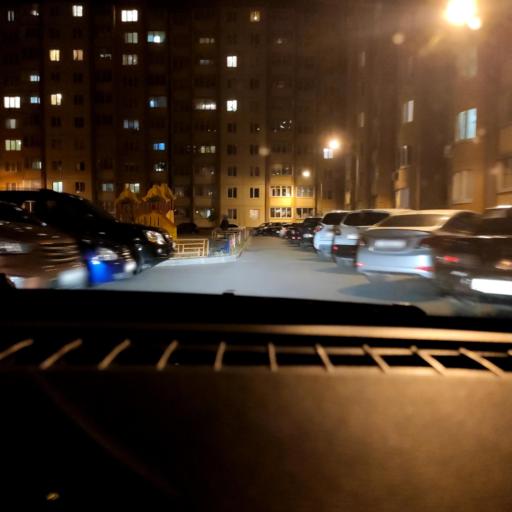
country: RU
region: Voronezj
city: Podgornoye
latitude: 51.7149
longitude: 39.1858
